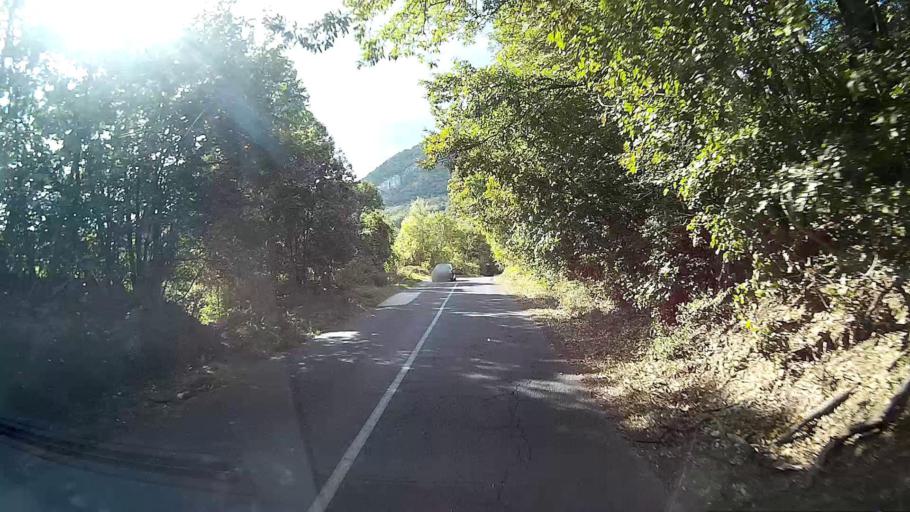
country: HU
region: Pest
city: Pilisszanto
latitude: 47.6793
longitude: 18.8898
